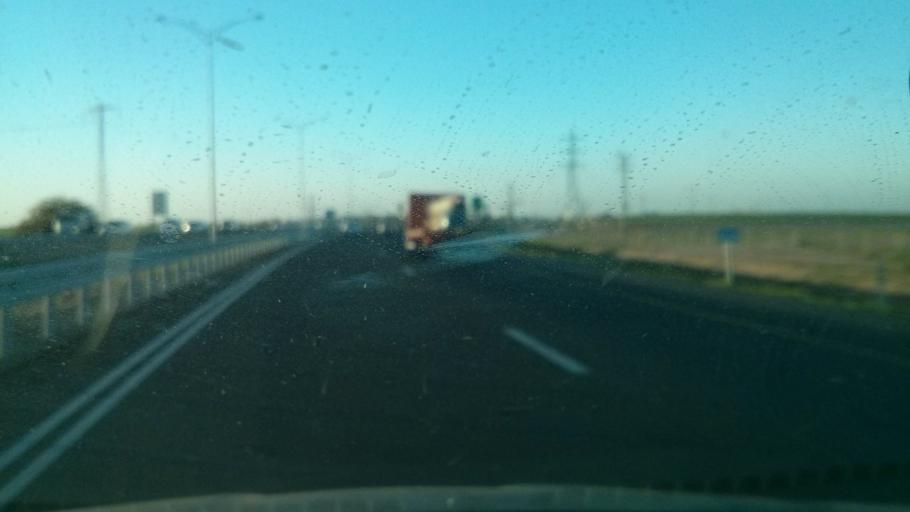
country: IL
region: Southern District
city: Lehavim
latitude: 31.4331
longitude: 34.7758
